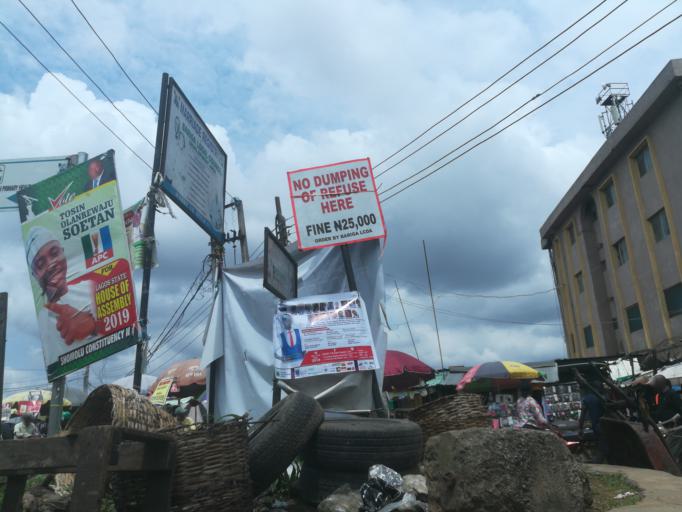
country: NG
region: Lagos
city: Somolu
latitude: 6.5374
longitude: 3.3921
